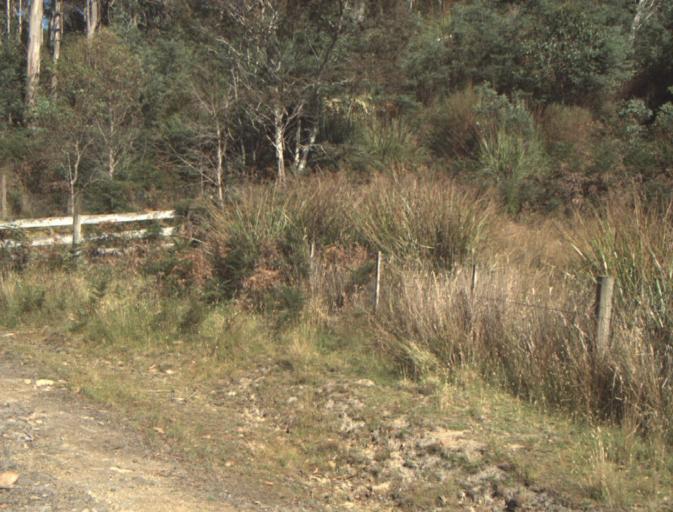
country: AU
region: Tasmania
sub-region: Launceston
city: Newstead
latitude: -41.3055
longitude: 147.3121
